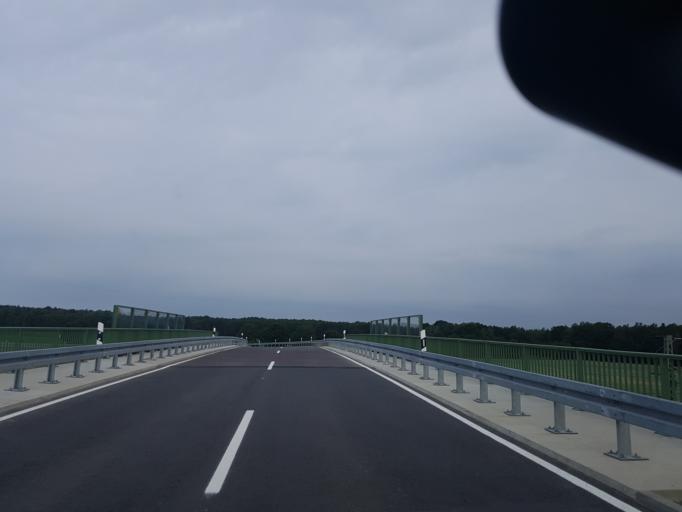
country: DE
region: Brandenburg
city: Schonewalde
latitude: 51.7059
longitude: 13.5980
